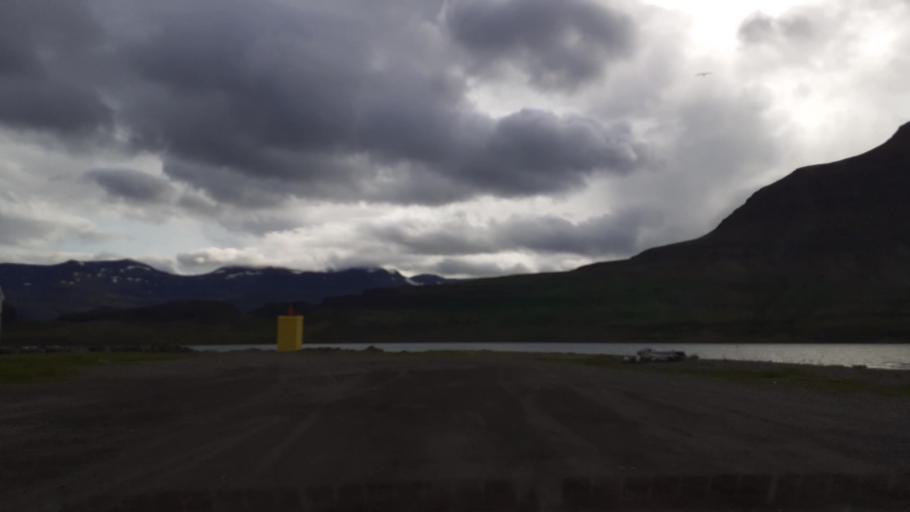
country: IS
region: East
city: Eskifjoerdur
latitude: 65.0601
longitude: -13.9931
